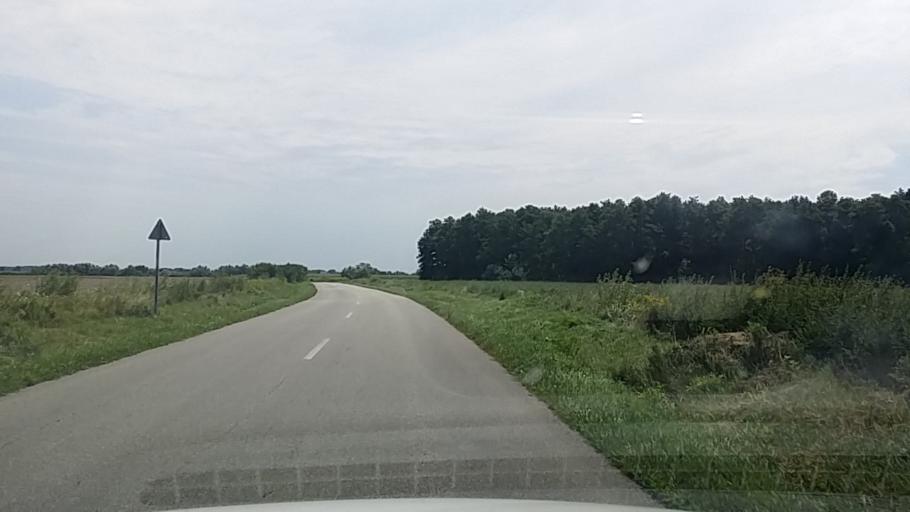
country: HU
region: Zala
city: Becsehely
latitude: 46.4098
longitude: 16.7790
